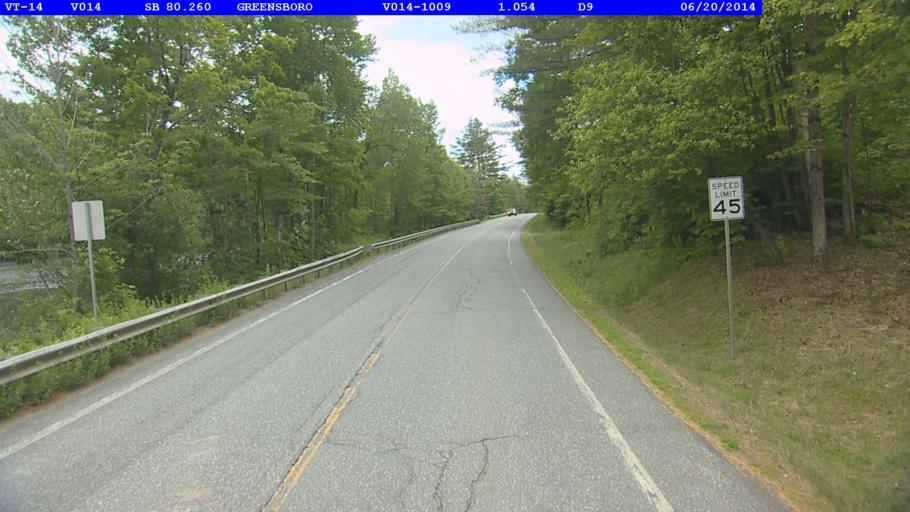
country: US
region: Vermont
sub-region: Caledonia County
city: Hardwick
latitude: 44.5943
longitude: -72.3582
